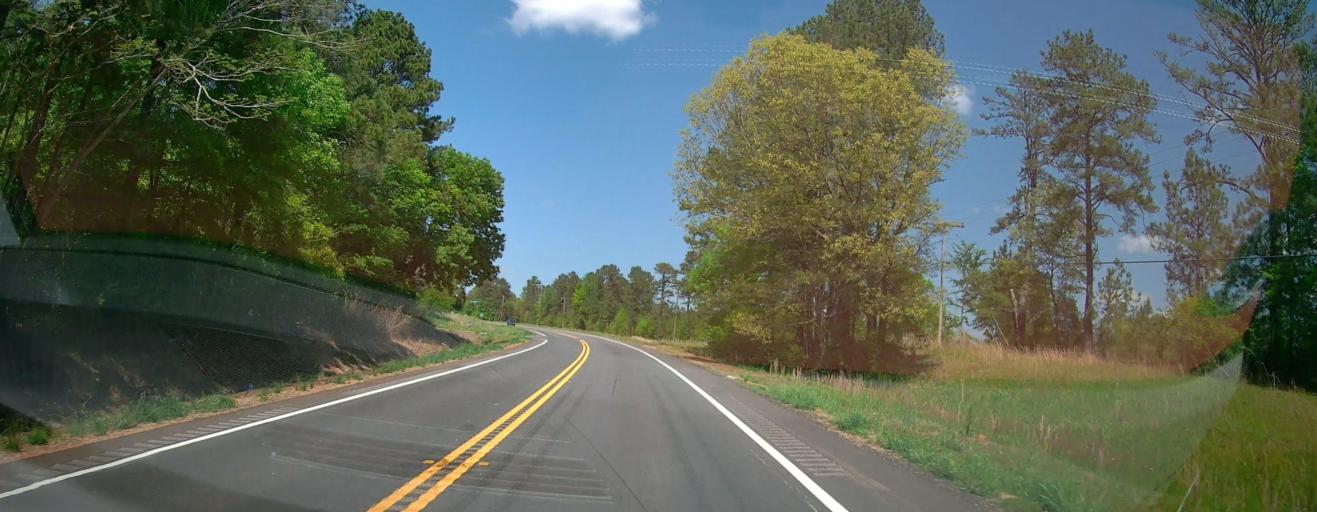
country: US
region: Georgia
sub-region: Putnam County
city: Eatonton
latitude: 33.2641
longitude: -83.4148
